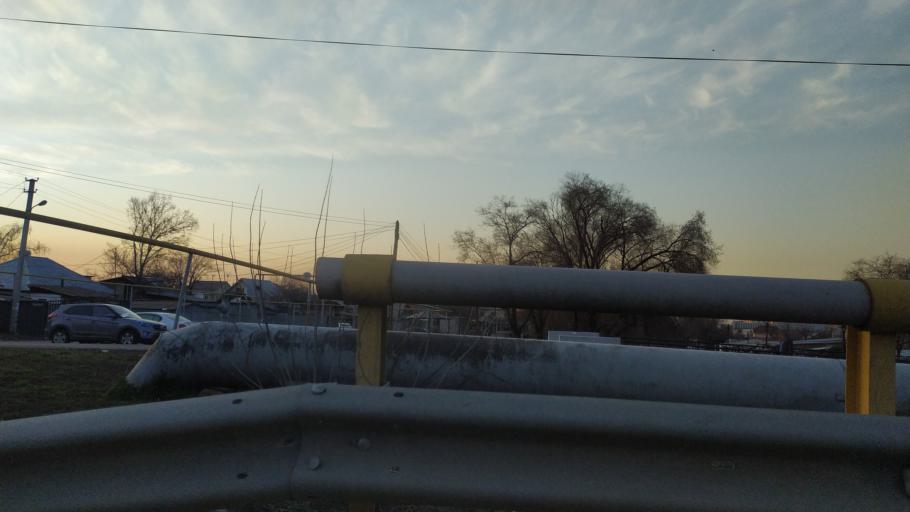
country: KZ
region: Almaty Qalasy
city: Almaty
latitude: 43.2214
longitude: 76.8825
